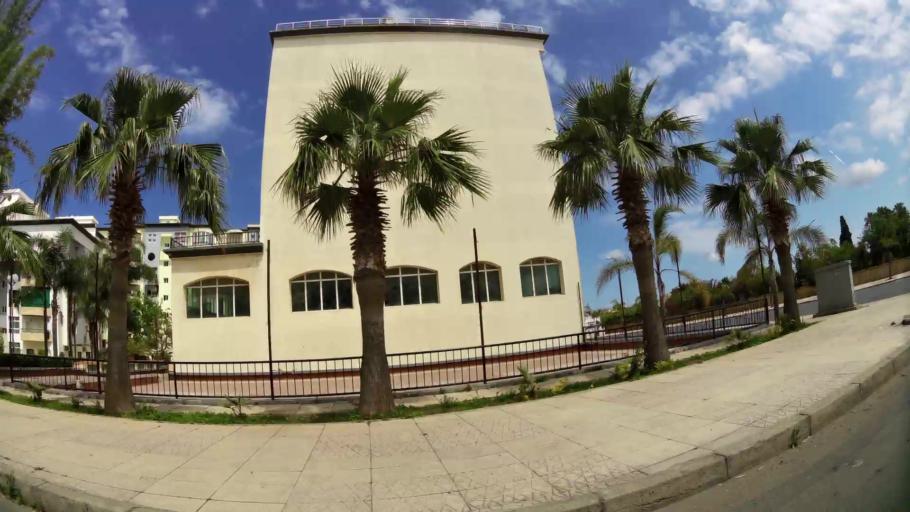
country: MA
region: Gharb-Chrarda-Beni Hssen
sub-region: Kenitra Province
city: Kenitra
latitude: 34.2516
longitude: -6.6010
